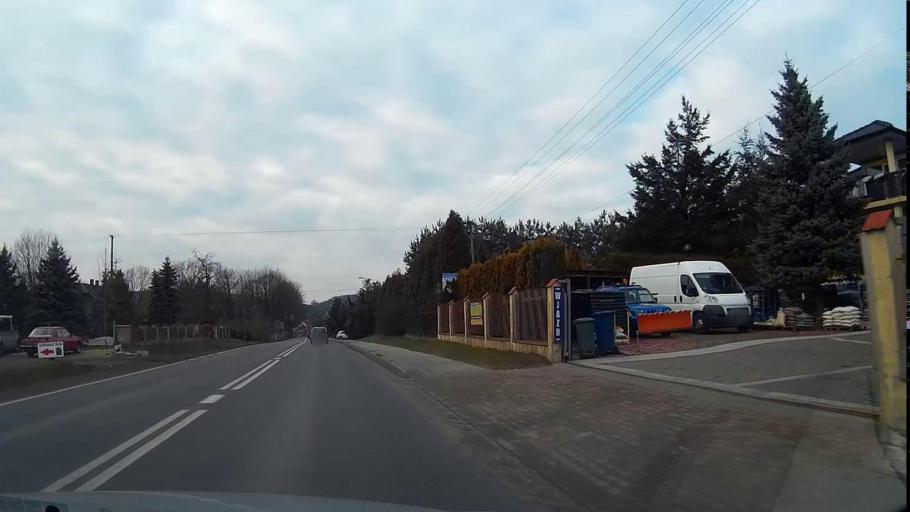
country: PL
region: Lesser Poland Voivodeship
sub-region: Powiat chrzanowski
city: Babice
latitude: 50.0733
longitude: 19.4406
